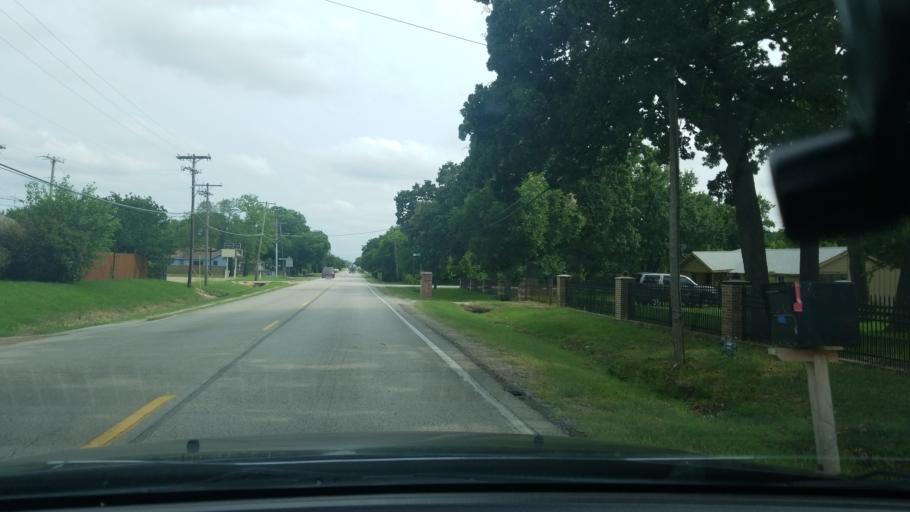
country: US
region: Texas
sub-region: Dallas County
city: Balch Springs
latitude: 32.7560
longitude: -96.6312
